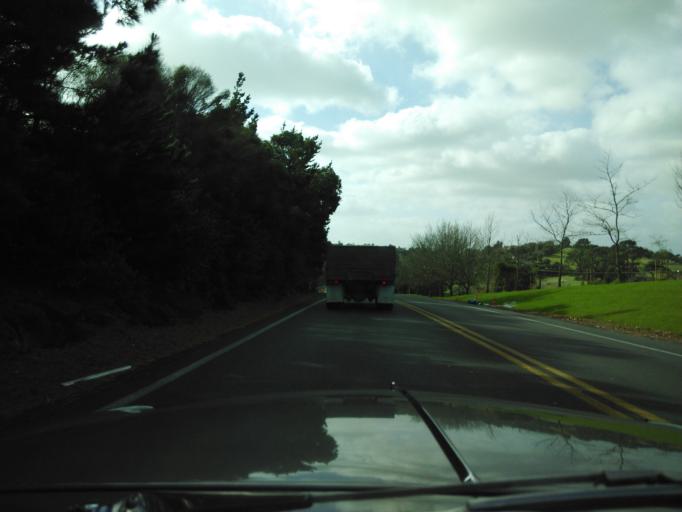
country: NZ
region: Auckland
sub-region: Auckland
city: Warkworth
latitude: -36.4120
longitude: 174.6578
